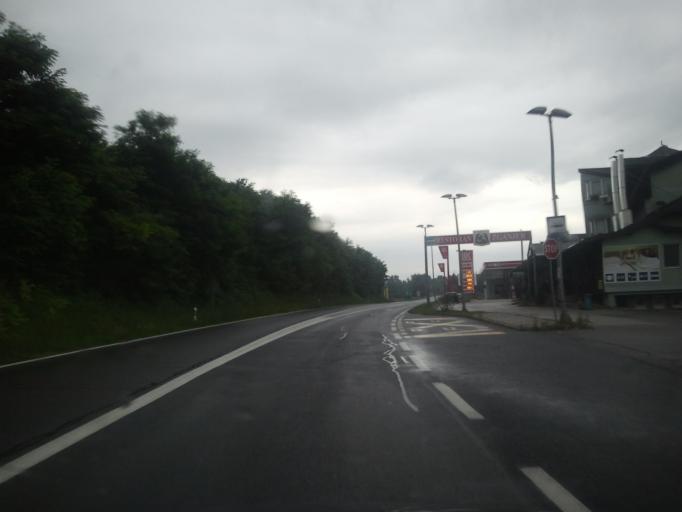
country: HR
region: Karlovacka
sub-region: Grad Karlovac
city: Karlovac
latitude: 45.4456
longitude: 15.5822
